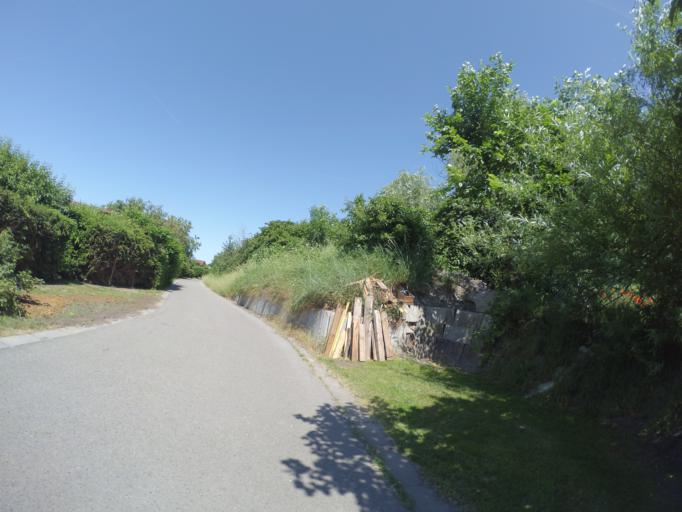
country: CZ
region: Central Bohemia
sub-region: Okres Nymburk
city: Nymburk
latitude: 50.1764
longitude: 15.0163
